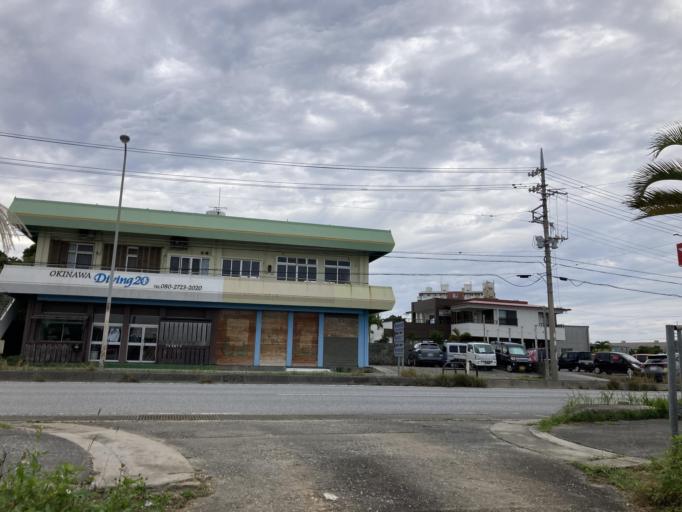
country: JP
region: Okinawa
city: Okinawa
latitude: 26.3923
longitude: 127.7556
